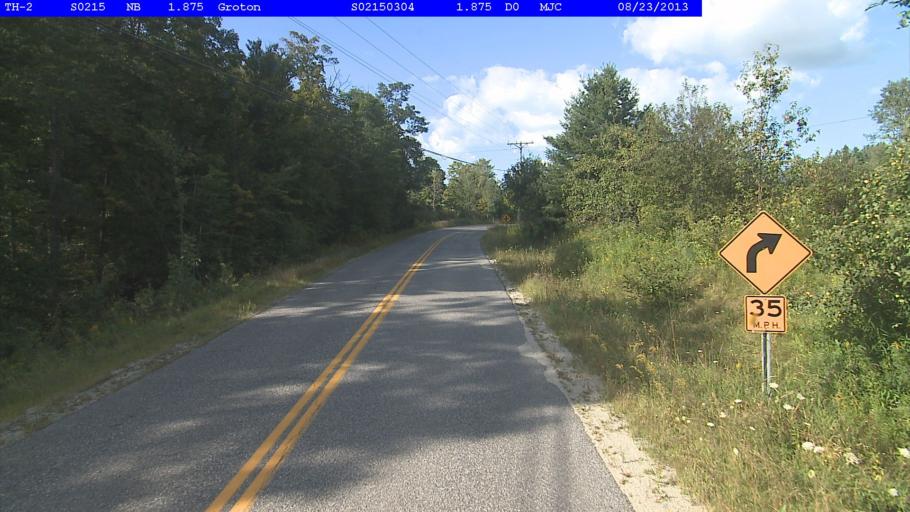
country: US
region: New Hampshire
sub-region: Grafton County
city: Woodsville
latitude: 44.2352
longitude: -72.1861
